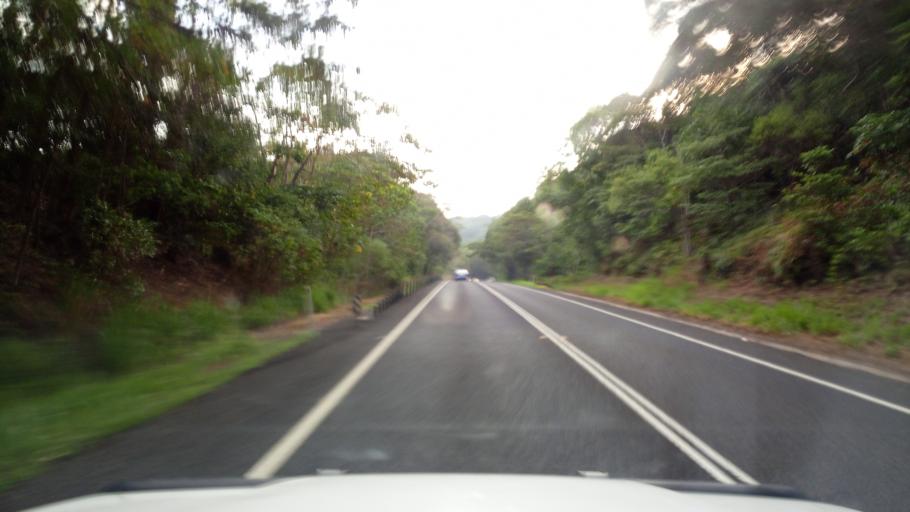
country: AU
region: Queensland
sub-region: Tablelands
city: Kuranda
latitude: -16.8388
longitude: 145.6164
